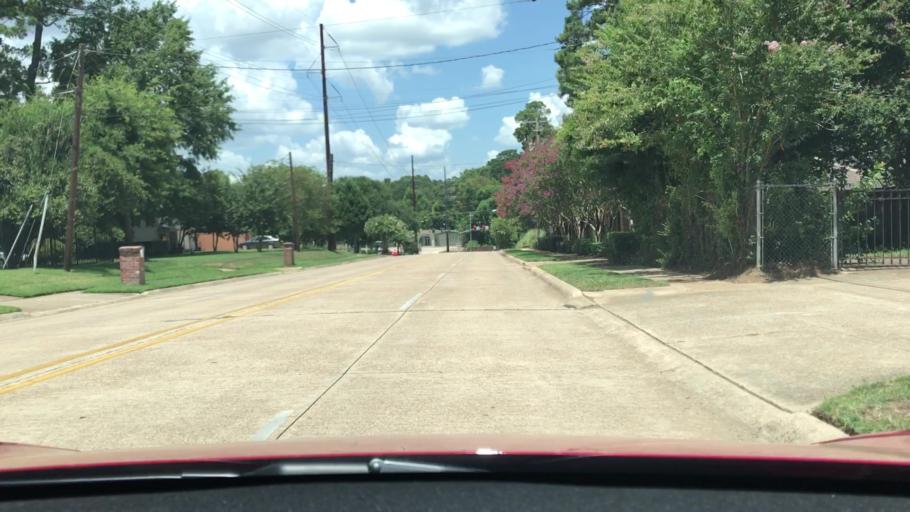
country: US
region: Louisiana
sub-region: Bossier Parish
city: Bossier City
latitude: 32.4413
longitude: -93.7374
